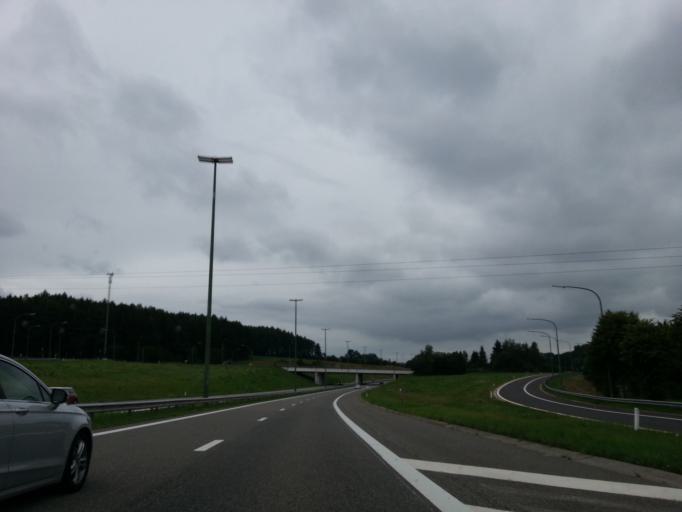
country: BE
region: Wallonia
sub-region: Province de Liege
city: Saint-Vith
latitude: 50.2647
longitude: 6.1174
